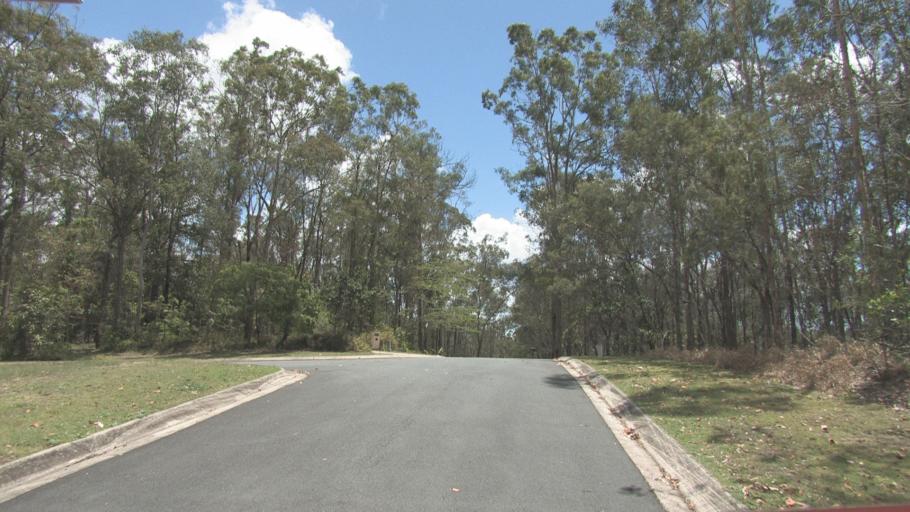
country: AU
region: Queensland
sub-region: Logan
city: Beenleigh
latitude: -27.6733
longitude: 153.2214
